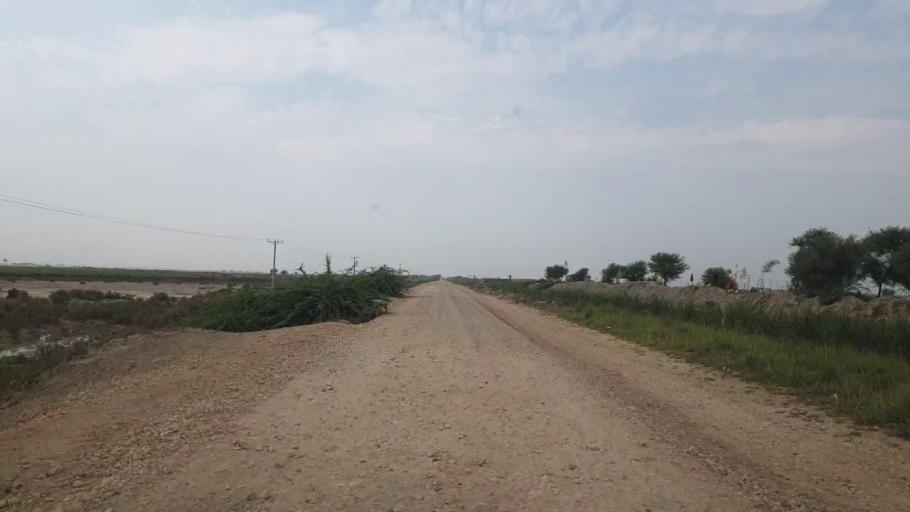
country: PK
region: Sindh
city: Kario
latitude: 24.6142
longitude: 68.5888
